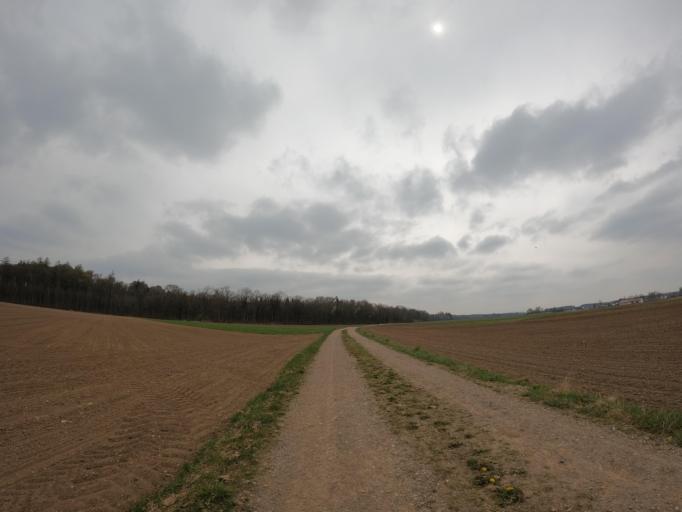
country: DE
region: Bavaria
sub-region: Upper Bavaria
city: Anzing
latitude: 48.1341
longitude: 11.8452
